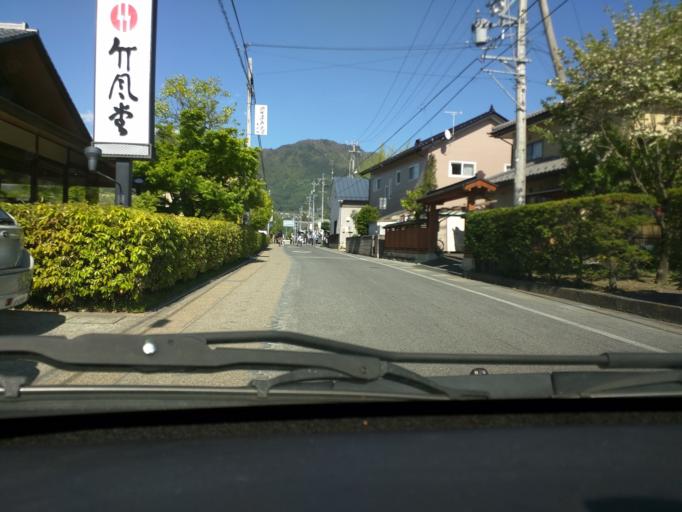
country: JP
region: Nagano
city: Nagano-shi
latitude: 36.5643
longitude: 138.1965
